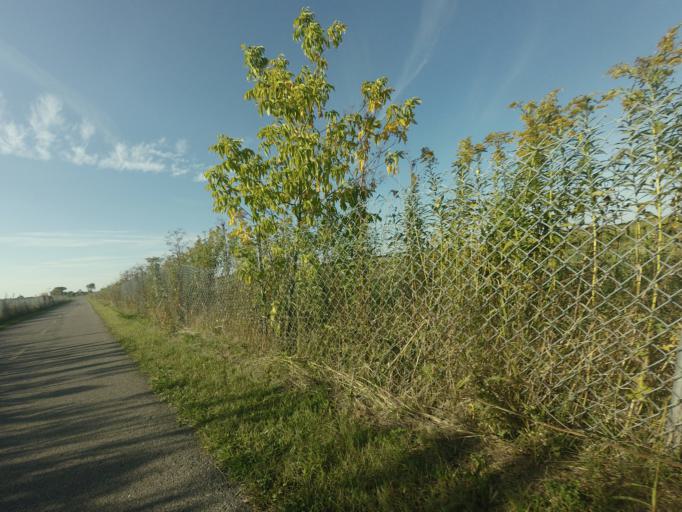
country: CA
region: Quebec
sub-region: Laurentides
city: Saint-Jerome
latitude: 45.7477
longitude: -73.9684
